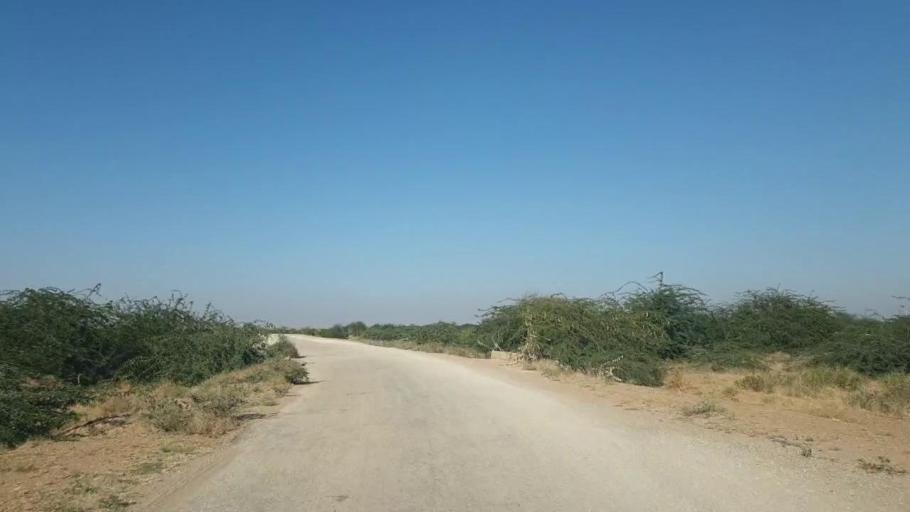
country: PK
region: Sindh
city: Malir Cantonment
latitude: 25.3316
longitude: 67.5721
